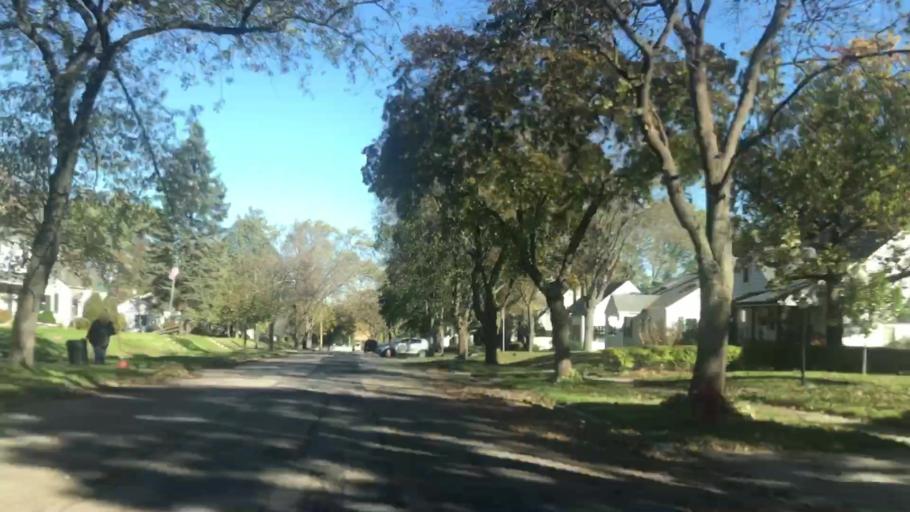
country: US
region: Wisconsin
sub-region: Waukesha County
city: Menomonee Falls
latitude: 43.1725
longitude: -88.1143
